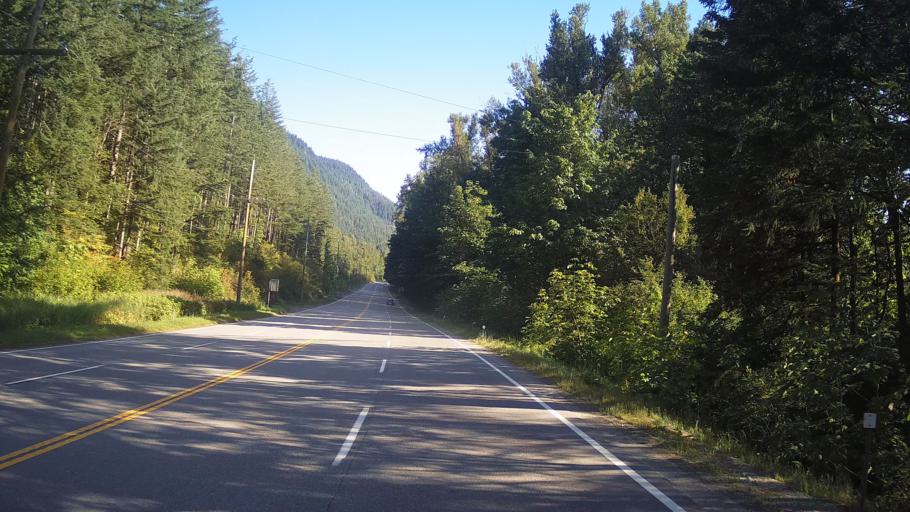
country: CA
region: British Columbia
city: Hope
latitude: 49.4422
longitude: -121.4364
